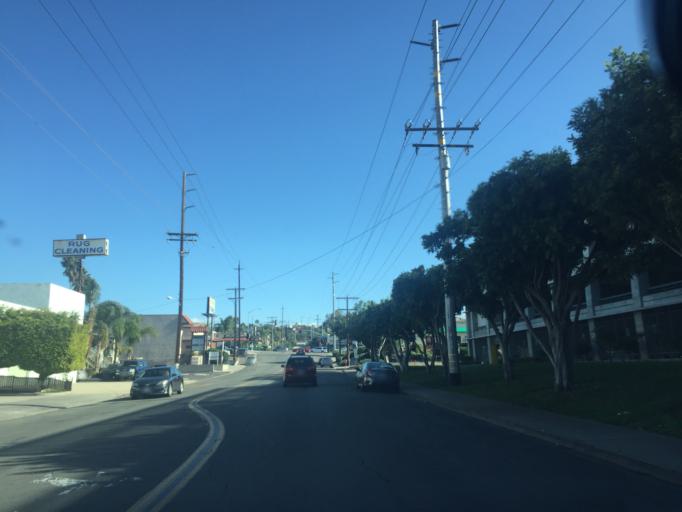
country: US
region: California
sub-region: San Diego County
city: La Mesa
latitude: 32.7878
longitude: -117.0992
